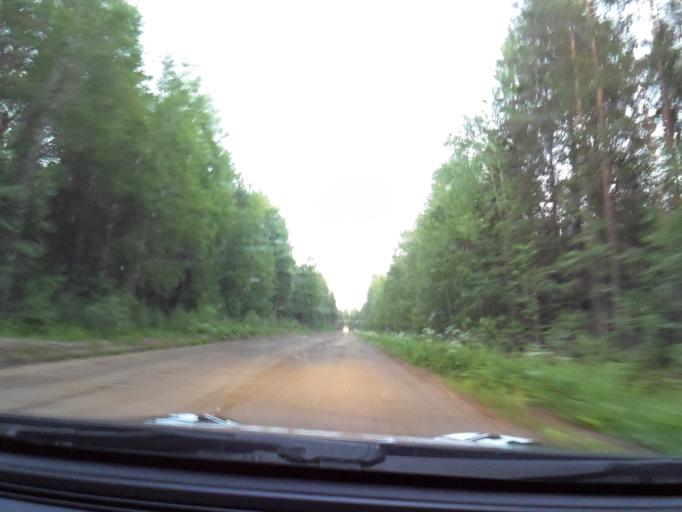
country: RU
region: Leningrad
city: Voznesen'ye
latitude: 60.8543
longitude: 35.9030
